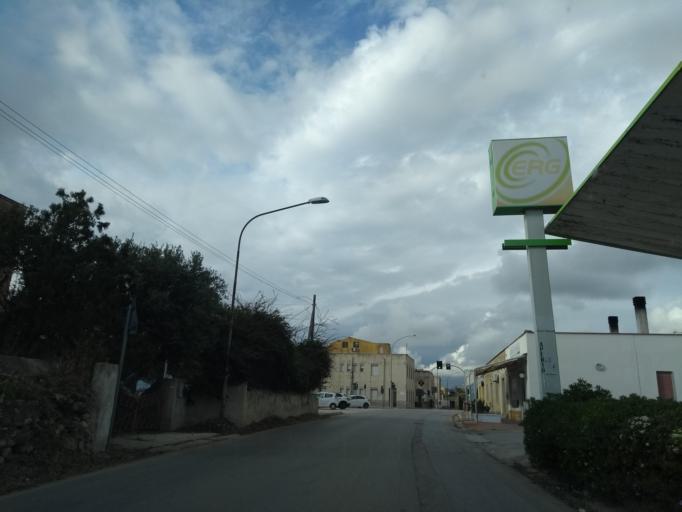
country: IT
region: Sicily
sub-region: Trapani
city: Marausa
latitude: 37.9505
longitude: 12.5140
